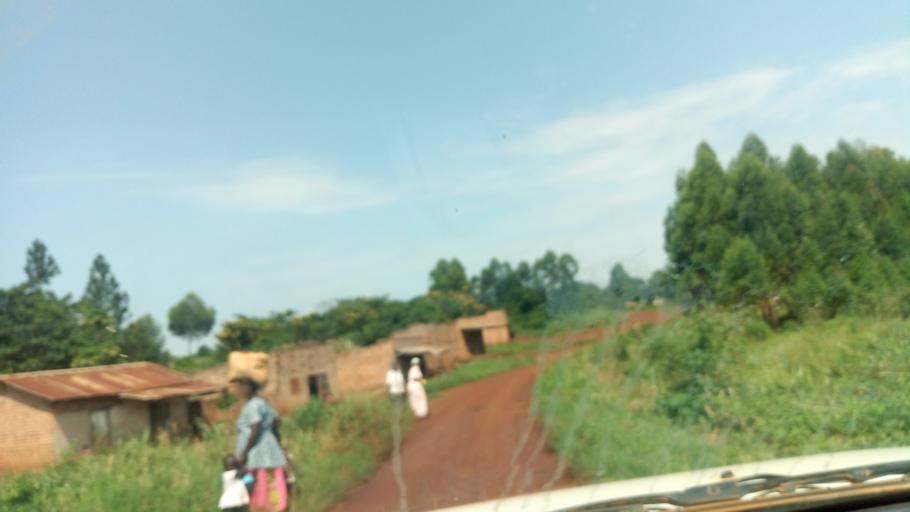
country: UG
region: Western Region
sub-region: Masindi District
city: Masindi
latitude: 1.6704
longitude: 31.8255
